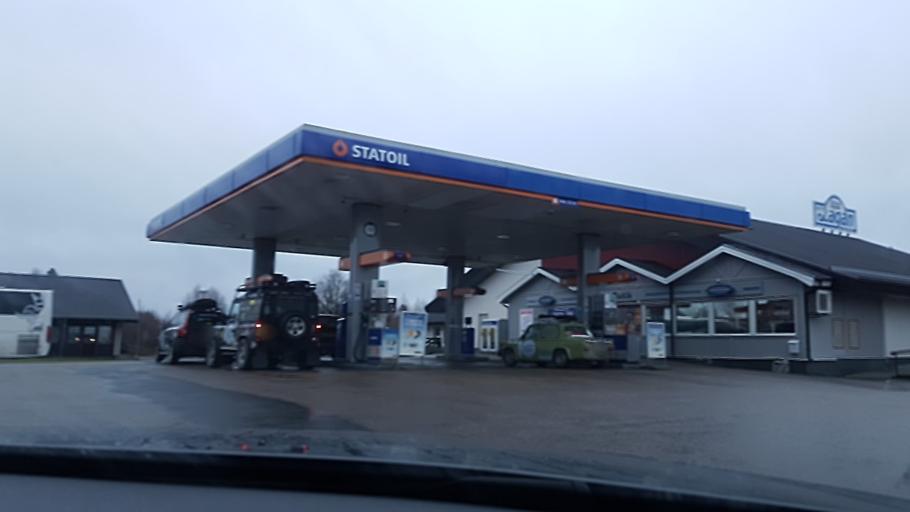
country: SE
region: Kronoberg
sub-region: Ljungby Kommun
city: Lagan
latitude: 56.9184
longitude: 13.9710
